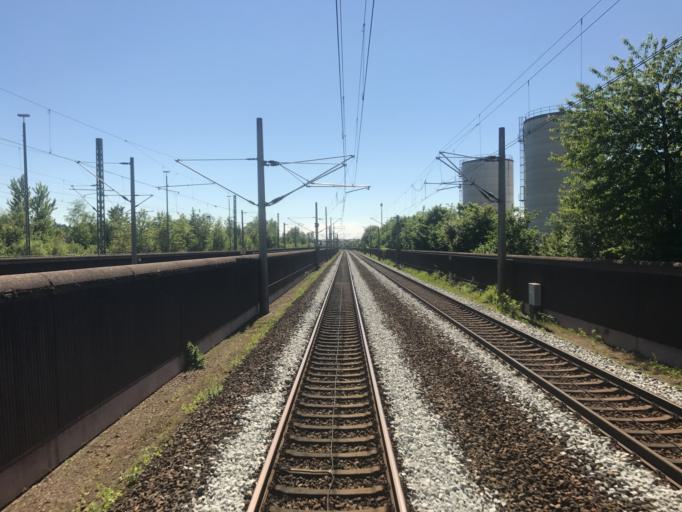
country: DE
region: Baden-Wuerttemberg
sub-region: Freiburg Region
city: Achern
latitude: 48.6316
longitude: 8.0601
